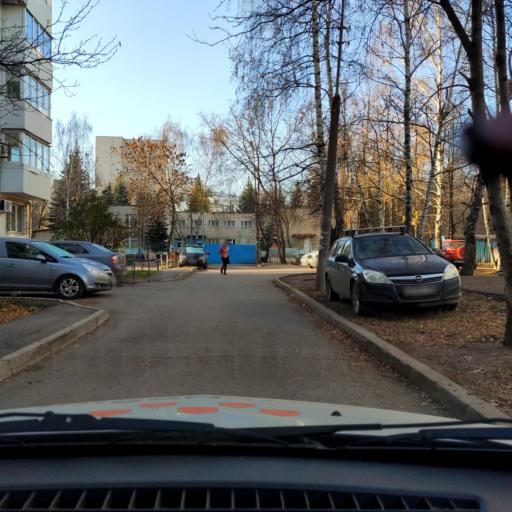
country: RU
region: Bashkortostan
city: Ufa
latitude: 54.7587
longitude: 55.9922
